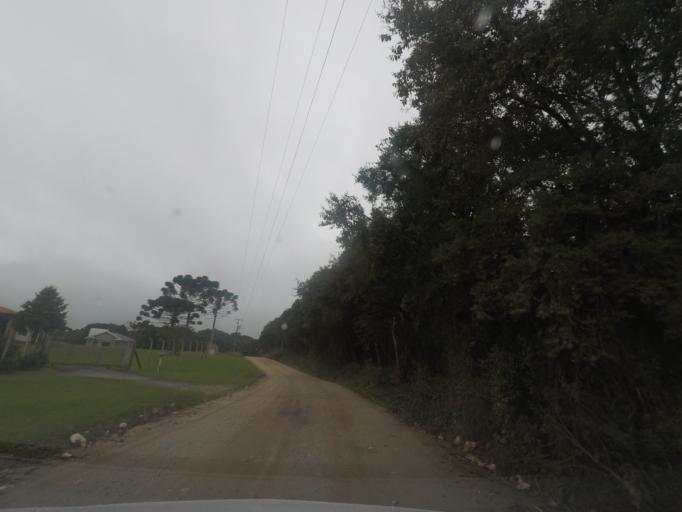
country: BR
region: Parana
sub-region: Campina Grande Do Sul
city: Campina Grande do Sul
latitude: -25.3092
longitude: -49.1018
